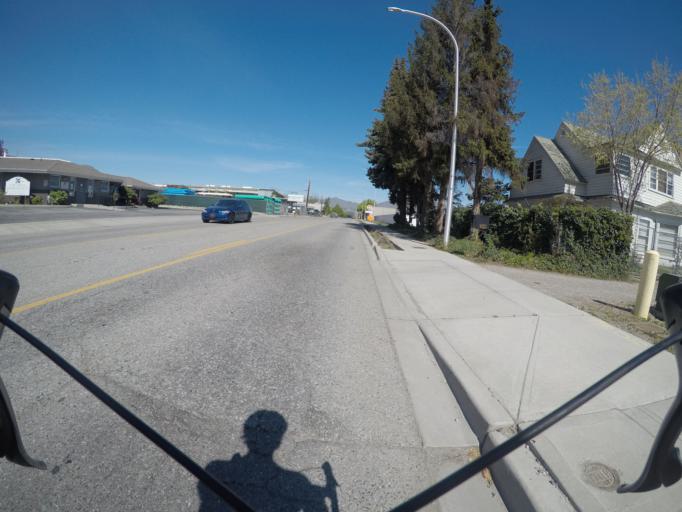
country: US
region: Washington
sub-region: Chelan County
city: Wenatchee
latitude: 47.4388
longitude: -120.3172
